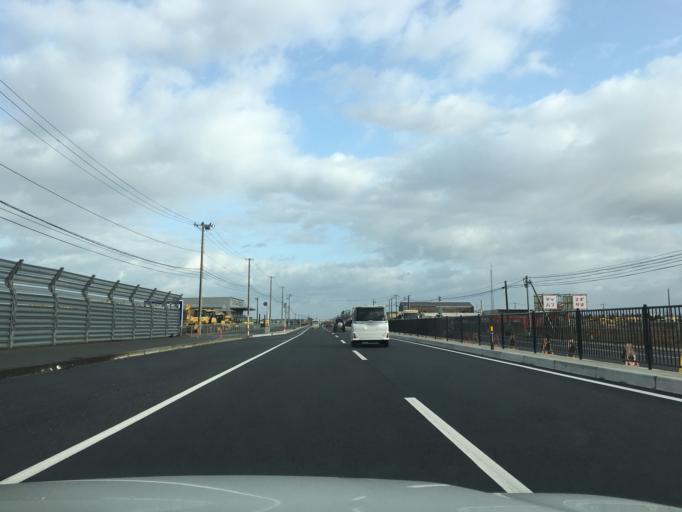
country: JP
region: Yamagata
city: Sakata
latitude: 38.8513
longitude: 139.8477
